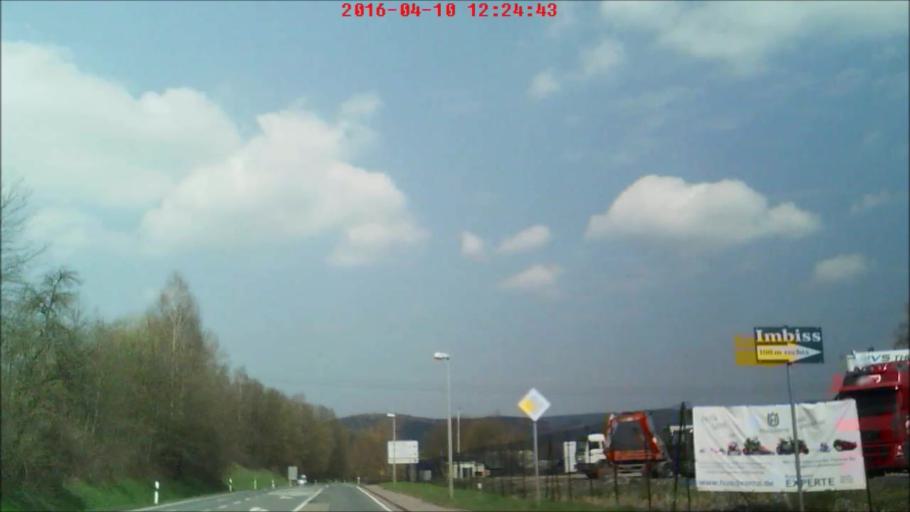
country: DE
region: Thuringia
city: Viernau
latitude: 50.6731
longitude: 10.5523
